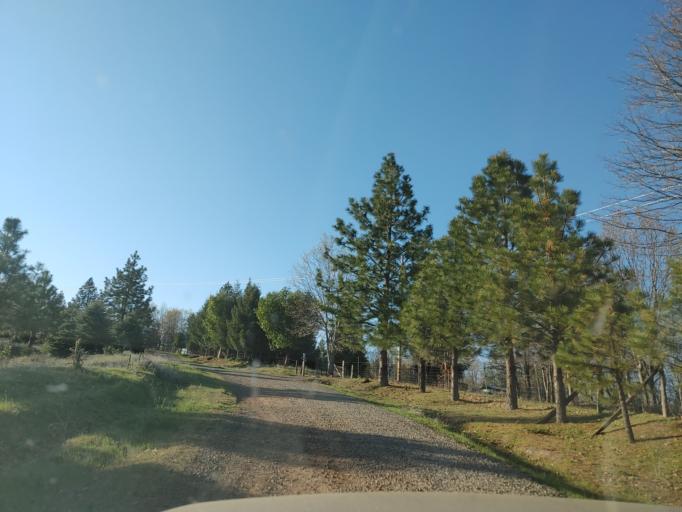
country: US
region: California
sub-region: Shasta County
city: Burney
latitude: 40.8097
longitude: -121.9420
